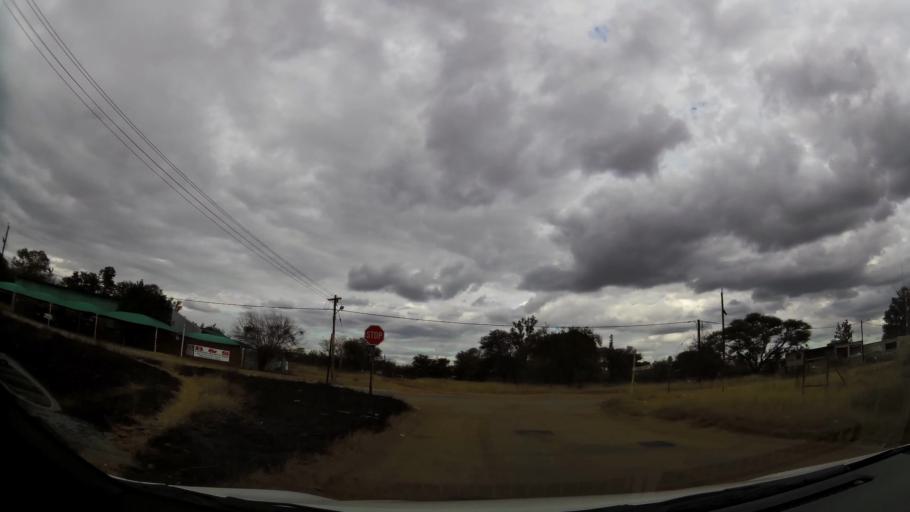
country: ZA
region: Limpopo
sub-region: Waterberg District Municipality
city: Modimolle
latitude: -24.7085
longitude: 28.4191
